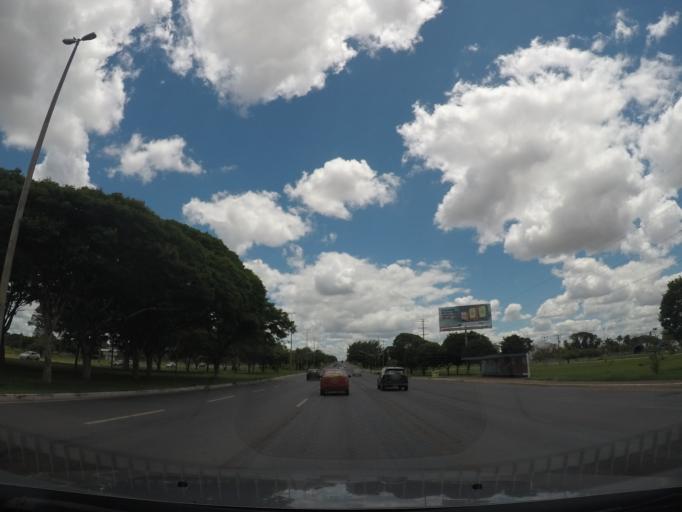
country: BR
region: Federal District
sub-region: Brasilia
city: Brasilia
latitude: -15.8156
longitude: -47.9496
